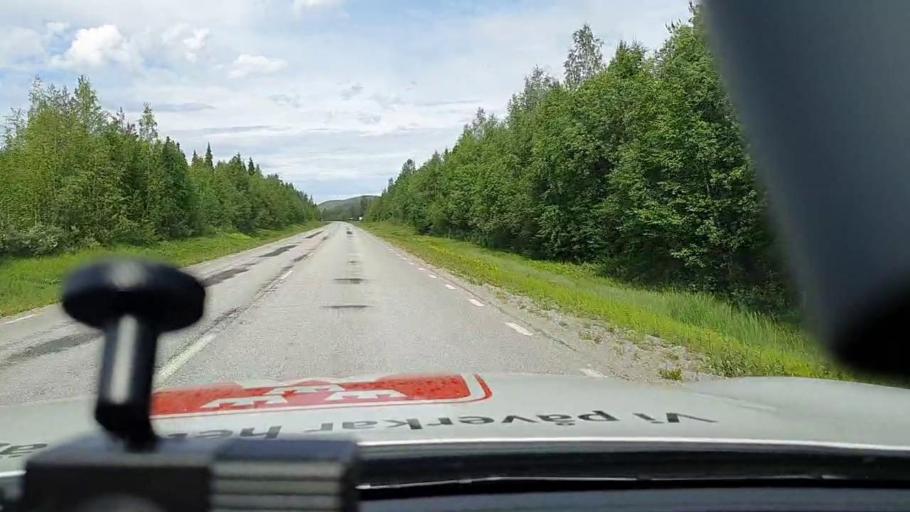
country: SE
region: Norrbotten
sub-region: Jokkmokks Kommun
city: Jokkmokk
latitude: 66.5498
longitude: 20.1236
